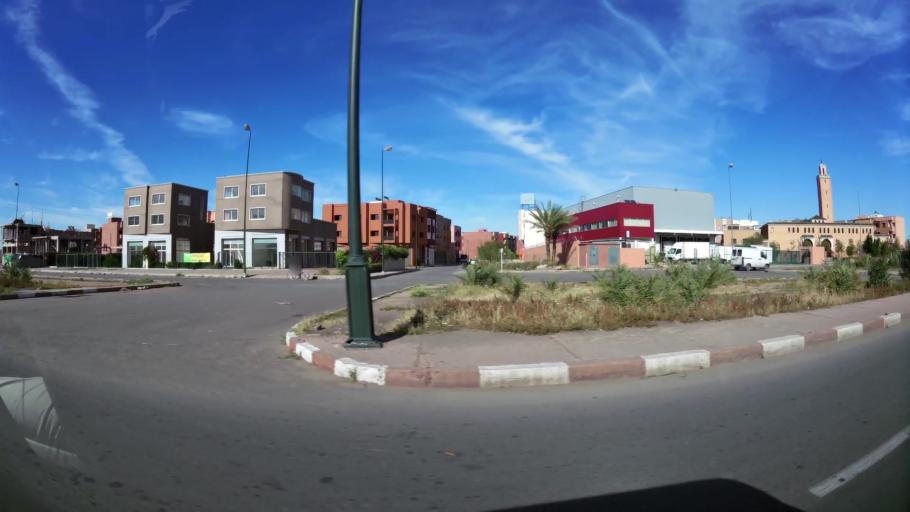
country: MA
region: Marrakech-Tensift-Al Haouz
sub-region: Marrakech
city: Marrakesh
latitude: 31.6793
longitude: -8.0480
